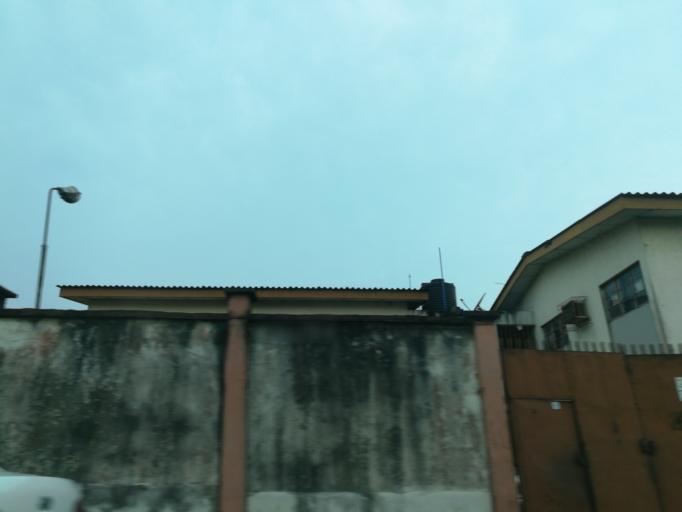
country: NG
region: Rivers
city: Port Harcourt
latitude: 4.8230
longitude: 7.0256
